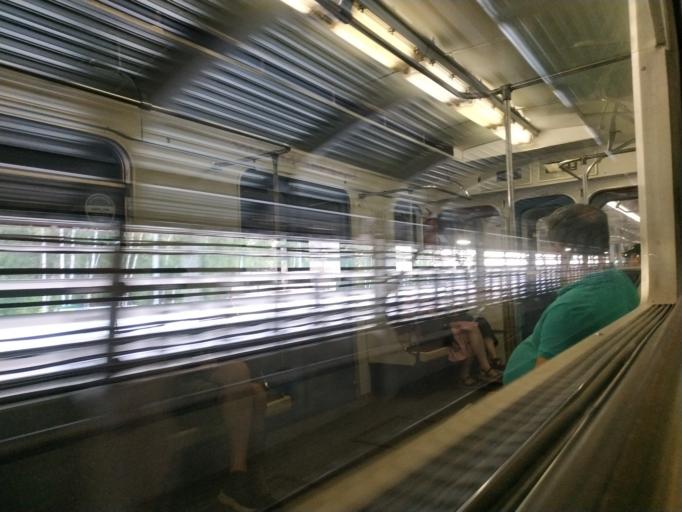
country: RU
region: Moskovskaya
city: Mosrentgen
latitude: 55.5958
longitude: 37.4166
